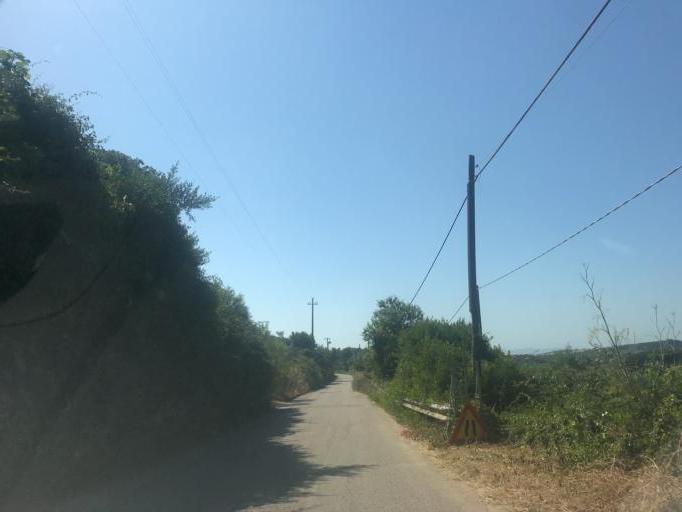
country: IT
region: Sardinia
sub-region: Provincia di Sassari
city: Alghero
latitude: 40.5507
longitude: 8.3669
